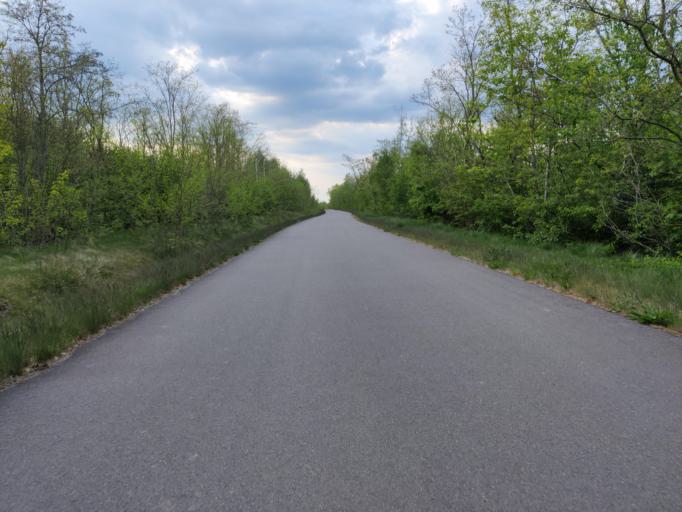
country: DE
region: Saxony
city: Espenhain
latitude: 51.2052
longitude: 12.4498
